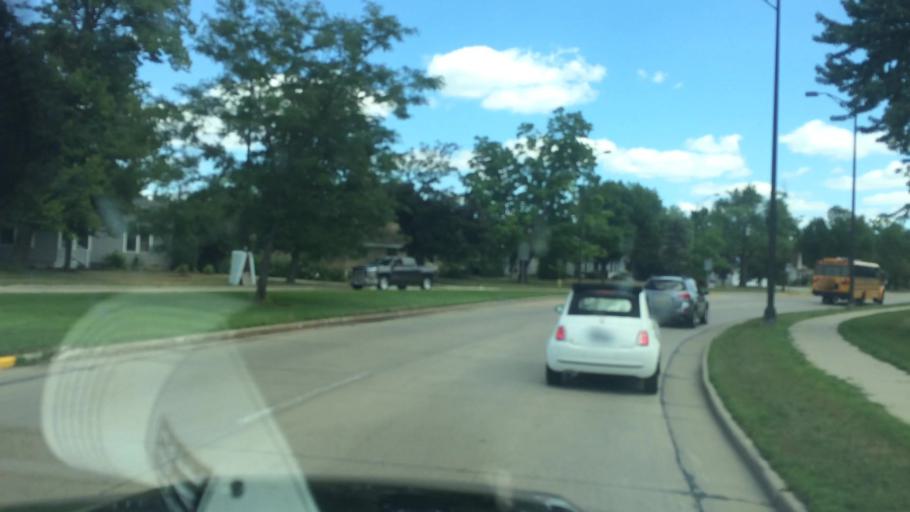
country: US
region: Wisconsin
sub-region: Portage County
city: Stevens Point
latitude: 44.5233
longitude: -89.5592
